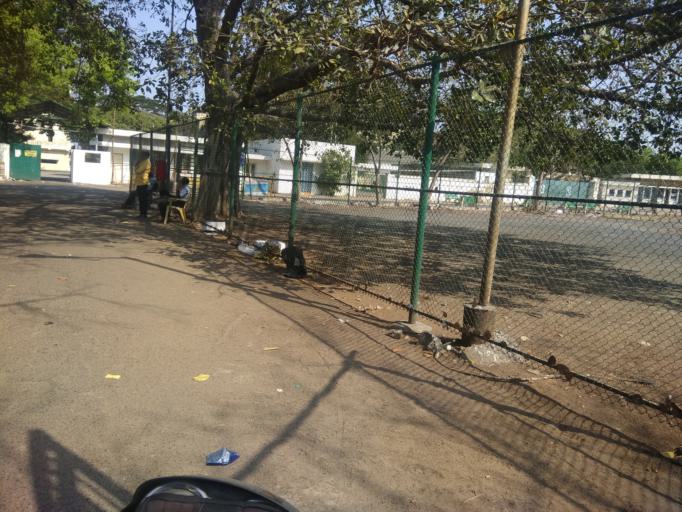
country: IN
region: Tamil Nadu
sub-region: Kancheepuram
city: Alandur
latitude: 13.0077
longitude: 80.2132
